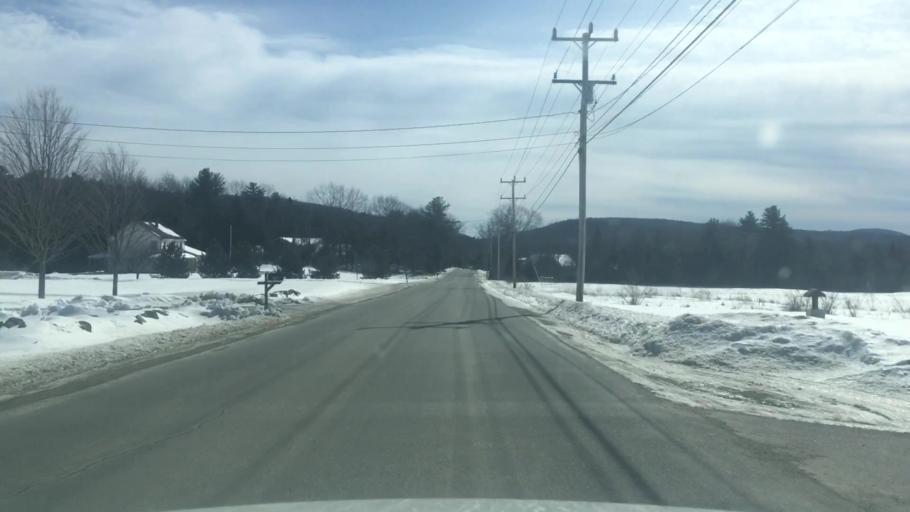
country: US
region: Maine
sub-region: Penobscot County
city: Holden
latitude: 44.7448
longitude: -68.6308
